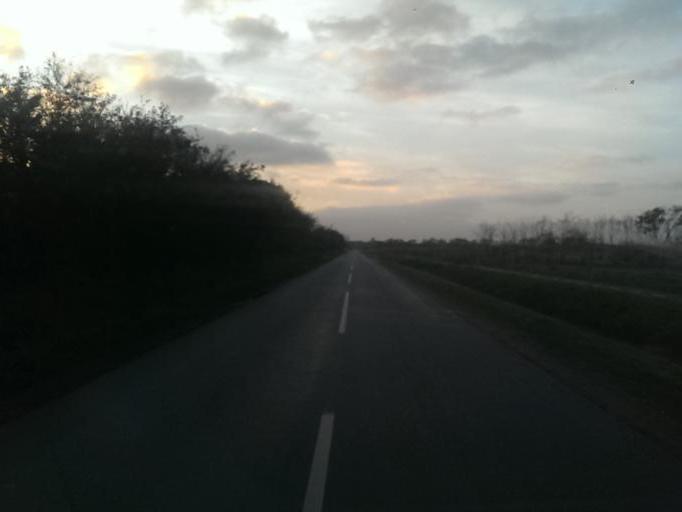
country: DK
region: South Denmark
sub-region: Esbjerg Kommune
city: Tjaereborg
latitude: 55.4585
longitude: 8.6110
